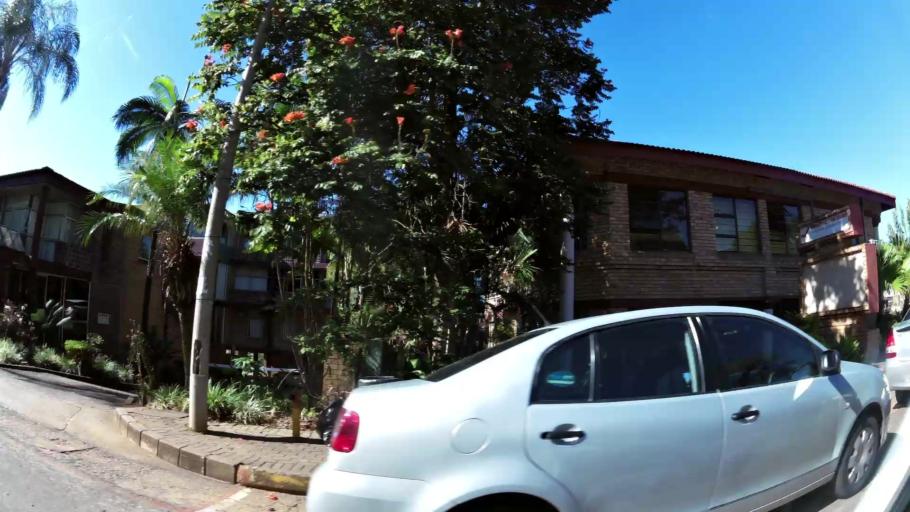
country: ZA
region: Limpopo
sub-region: Mopani District Municipality
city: Tzaneen
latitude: -23.8313
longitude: 30.1583
